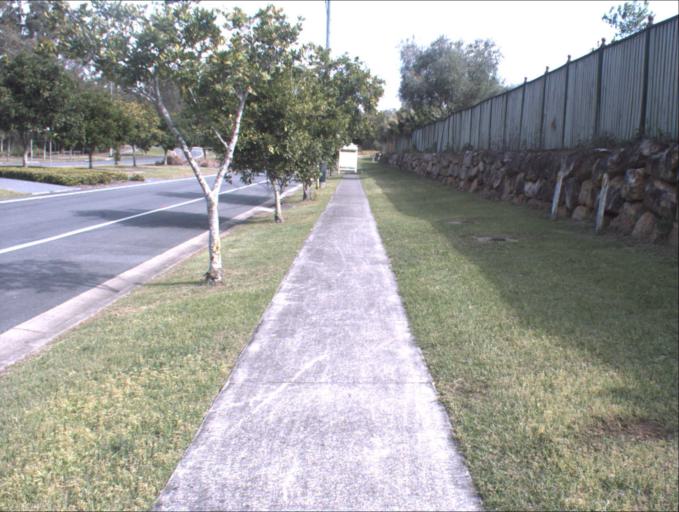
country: AU
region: Queensland
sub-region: Logan
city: Park Ridge South
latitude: -27.6889
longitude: 153.0569
